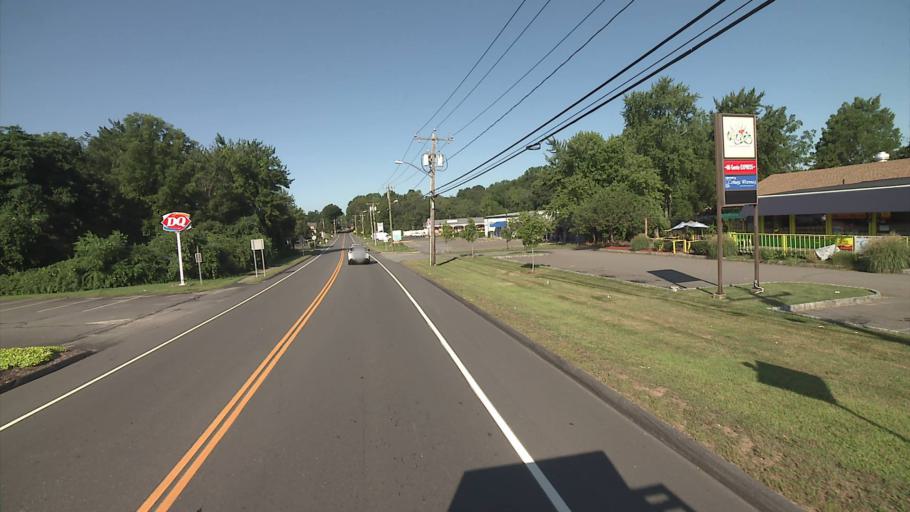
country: US
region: Connecticut
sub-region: Middlesex County
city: Saybrook Manor
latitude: 41.2873
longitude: -72.4048
